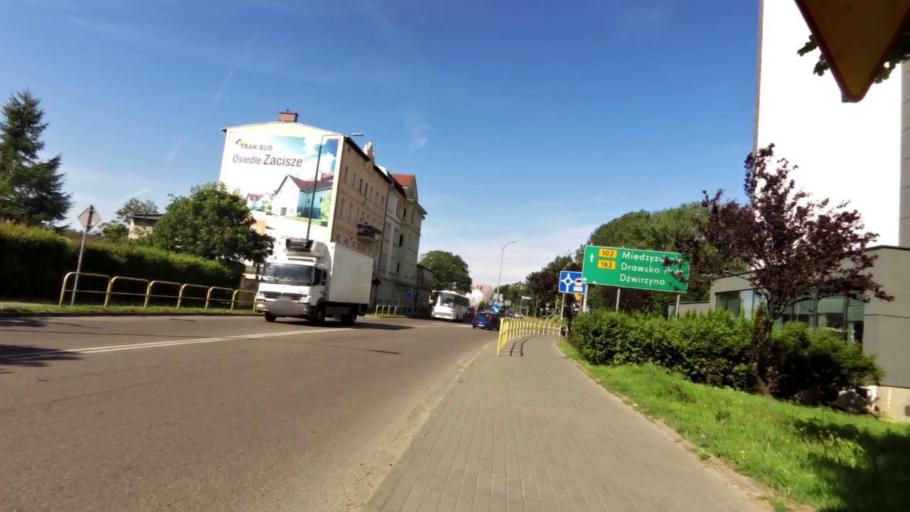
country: PL
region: West Pomeranian Voivodeship
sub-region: Powiat kolobrzeski
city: Kolobrzeg
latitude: 54.1727
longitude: 15.5741
